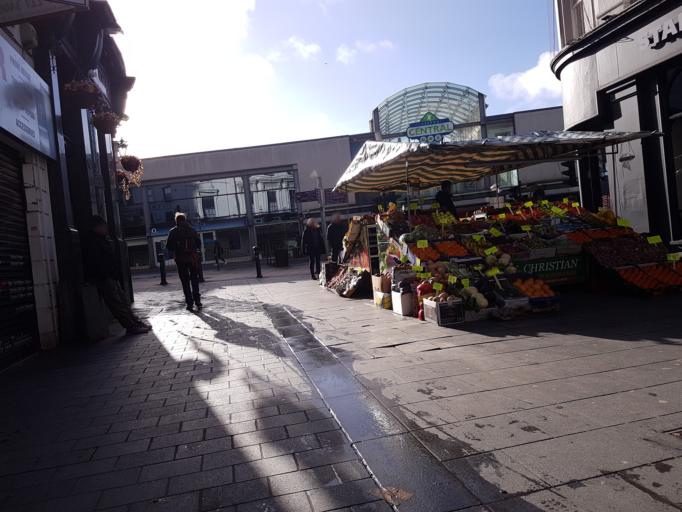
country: GB
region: England
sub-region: Liverpool
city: Liverpool
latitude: 53.4052
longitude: -2.9807
